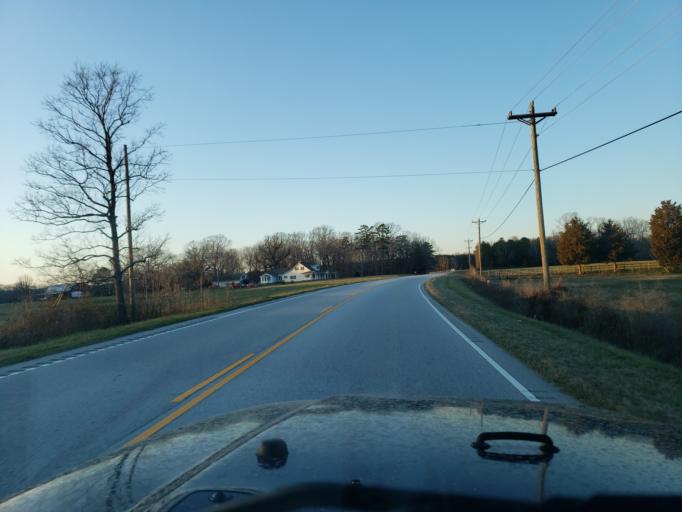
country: US
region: South Carolina
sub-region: York County
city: Clover
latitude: 35.1316
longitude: -81.3111
